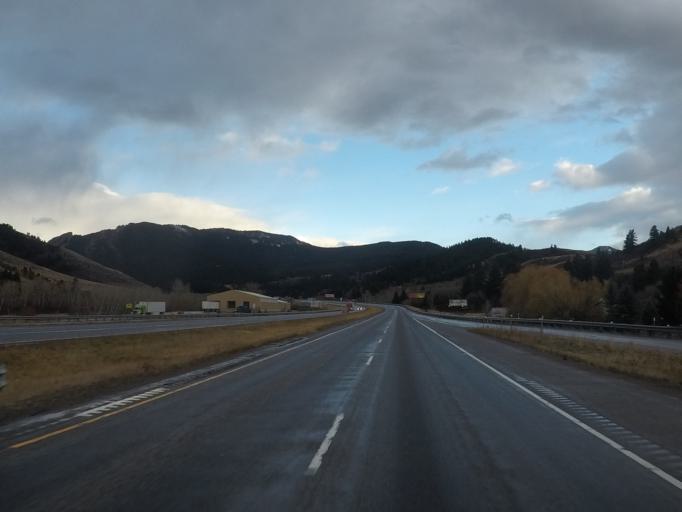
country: US
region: Montana
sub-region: Gallatin County
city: Bozeman
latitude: 45.6525
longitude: -110.9440
